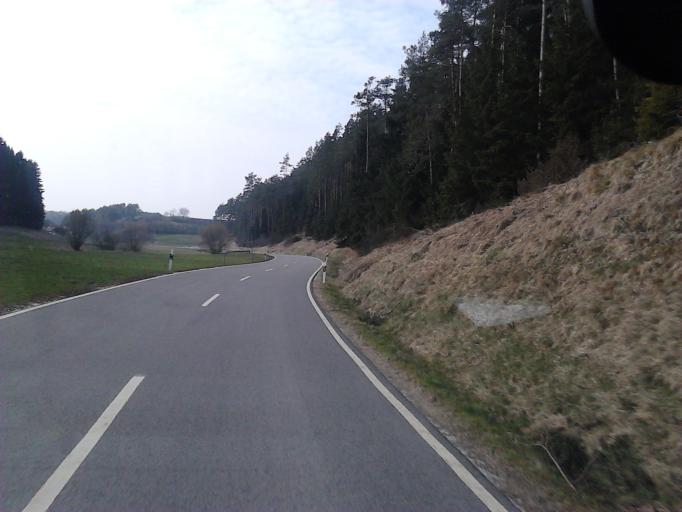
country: DE
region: Bavaria
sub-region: Upper Franconia
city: Stadelhofen
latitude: 49.9741
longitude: 11.1892
